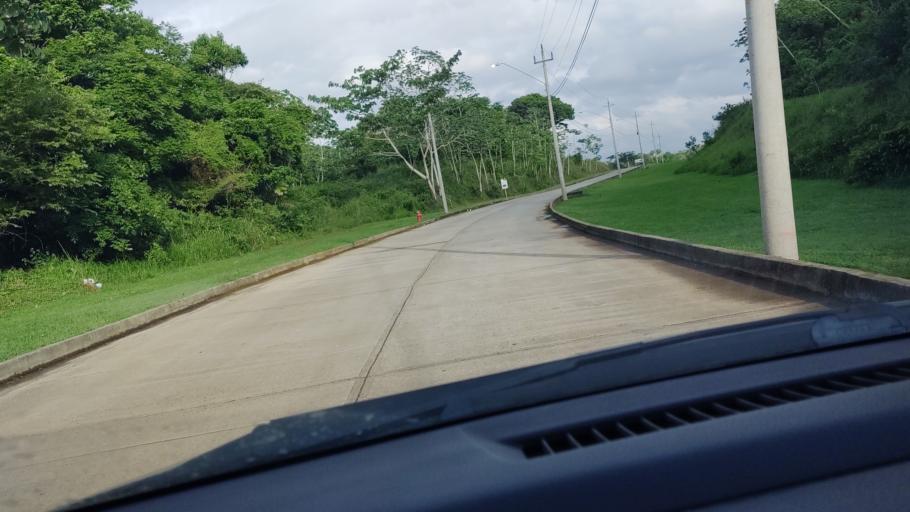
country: PA
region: Panama
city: Nuevo Arraijan
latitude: 8.9251
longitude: -79.7544
